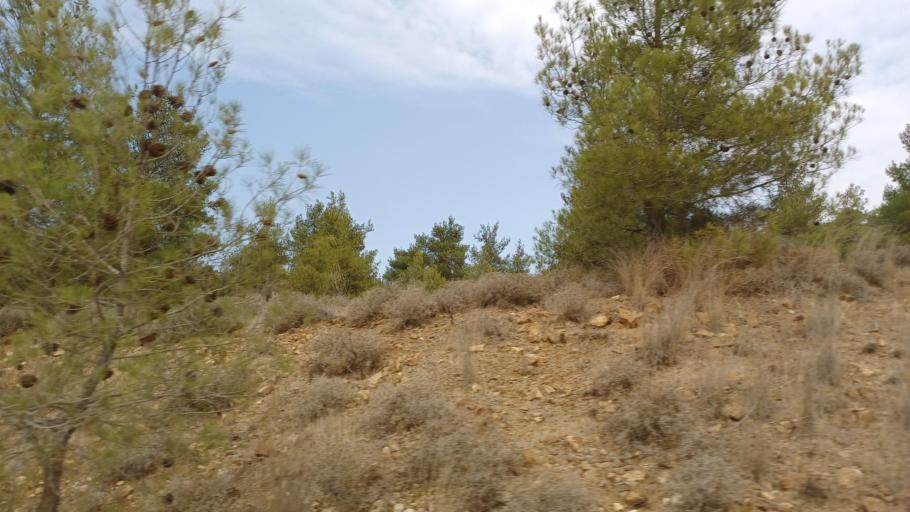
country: CY
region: Lefkosia
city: Klirou
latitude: 35.0407
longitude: 33.1096
